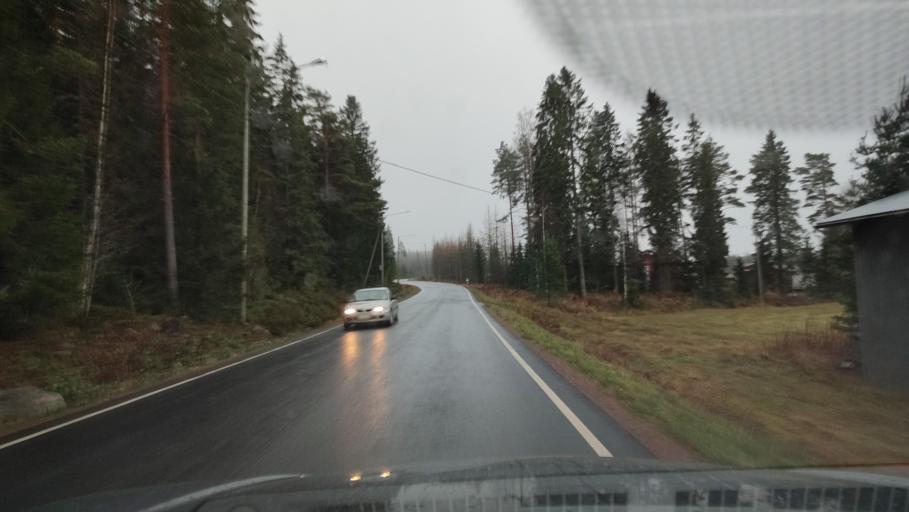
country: FI
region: Southern Ostrobothnia
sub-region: Suupohja
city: Karijoki
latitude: 62.1411
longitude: 21.6854
